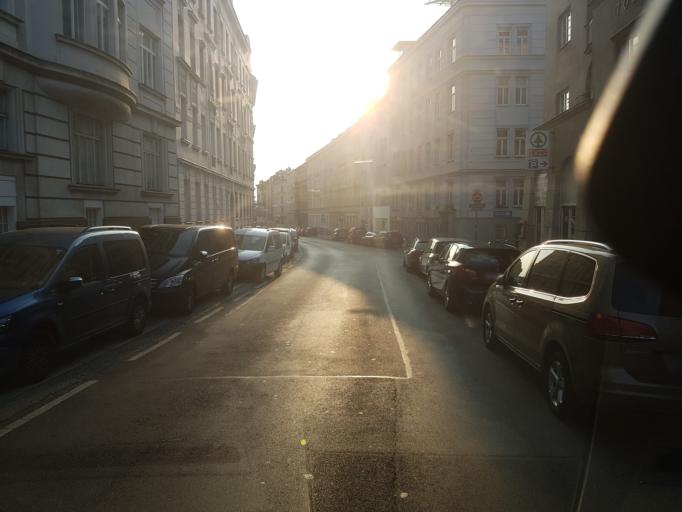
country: AT
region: Vienna
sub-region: Wien Stadt
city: Vienna
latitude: 48.2288
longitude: 16.3318
